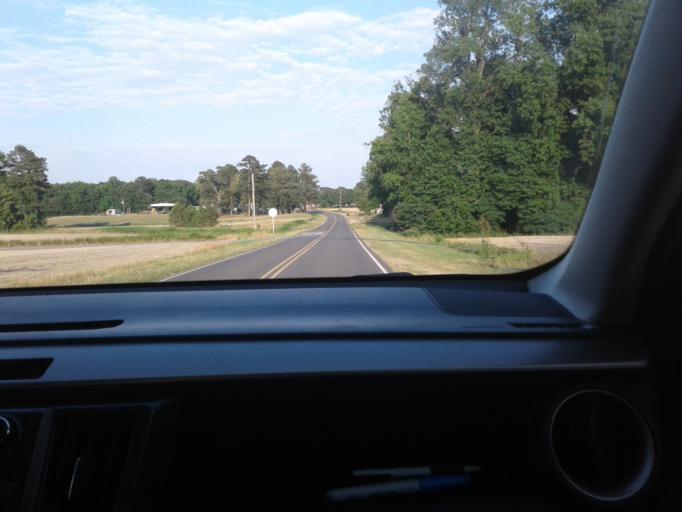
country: US
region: North Carolina
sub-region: Harnett County
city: Dunn
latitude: 35.3353
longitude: -78.5867
